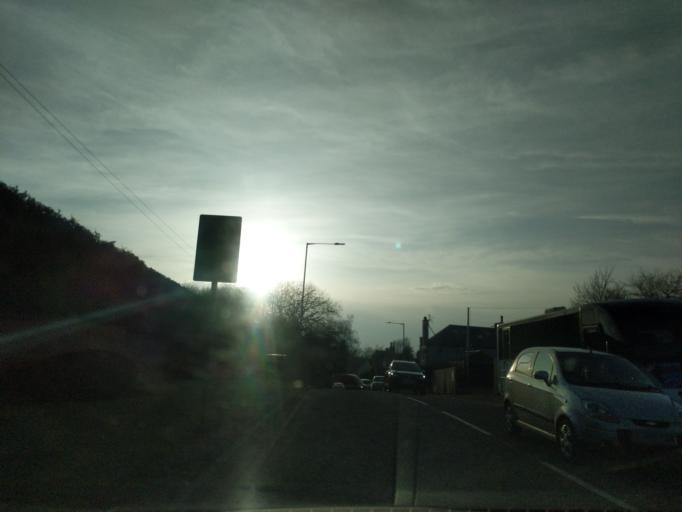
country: GB
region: Scotland
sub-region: South Lanarkshire
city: Carluke
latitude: 55.7319
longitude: -3.8371
